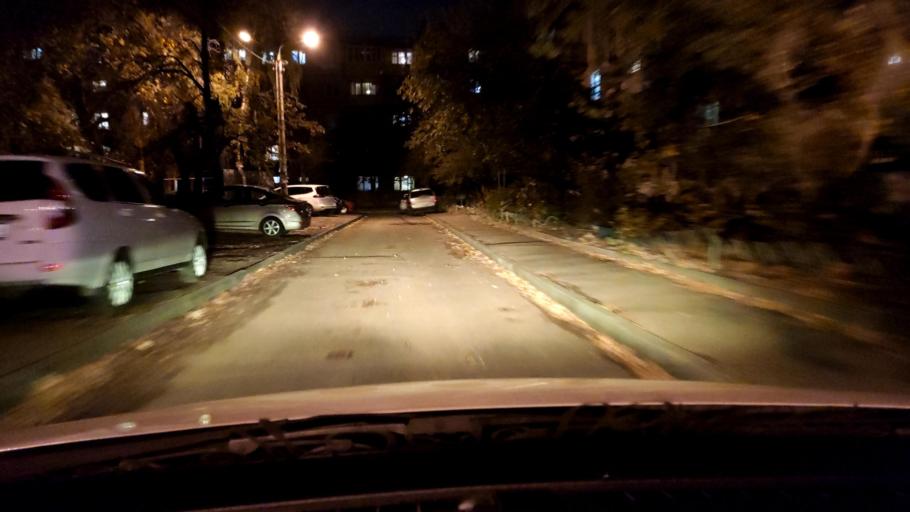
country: RU
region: Voronezj
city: Pridonskoy
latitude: 51.6558
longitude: 39.1096
